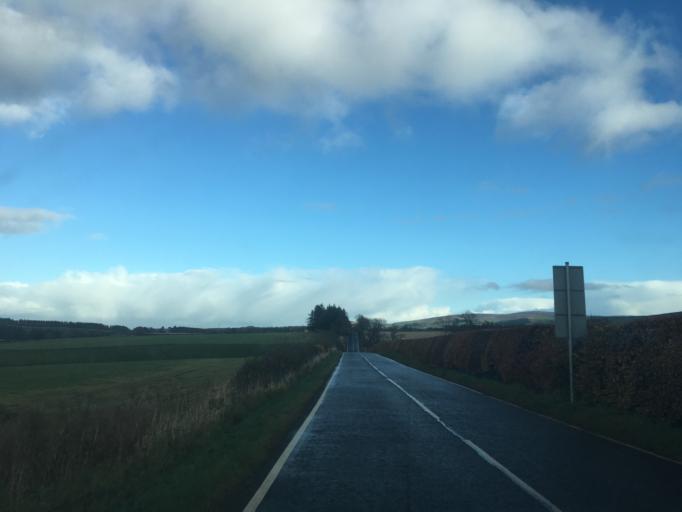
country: GB
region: Scotland
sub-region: East Lothian
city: Pencaitland
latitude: 55.8405
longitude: -2.8929
